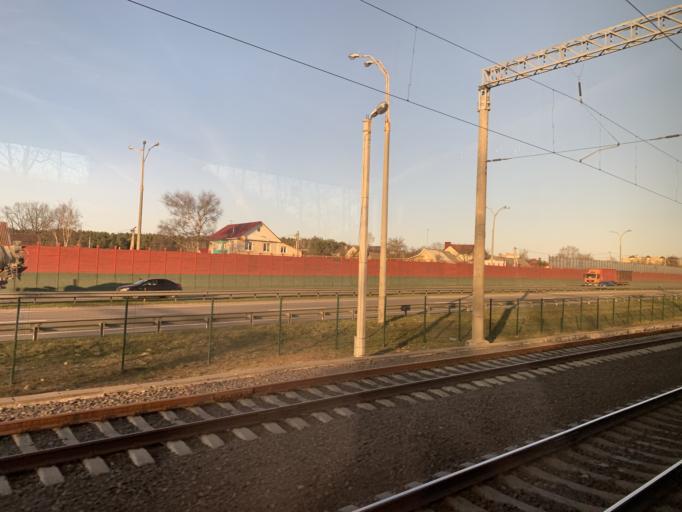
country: BY
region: Minsk
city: Zhdanovichy
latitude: 53.9501
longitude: 27.4176
